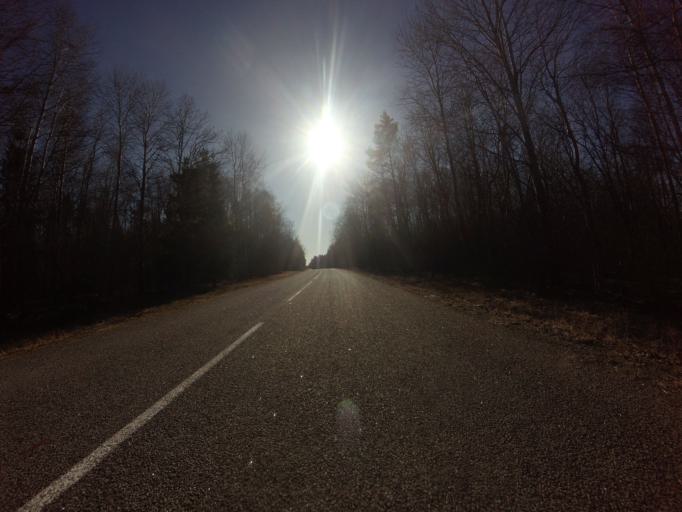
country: EE
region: Saare
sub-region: Kuressaare linn
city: Kuressaare
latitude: 58.4742
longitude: 22.2448
